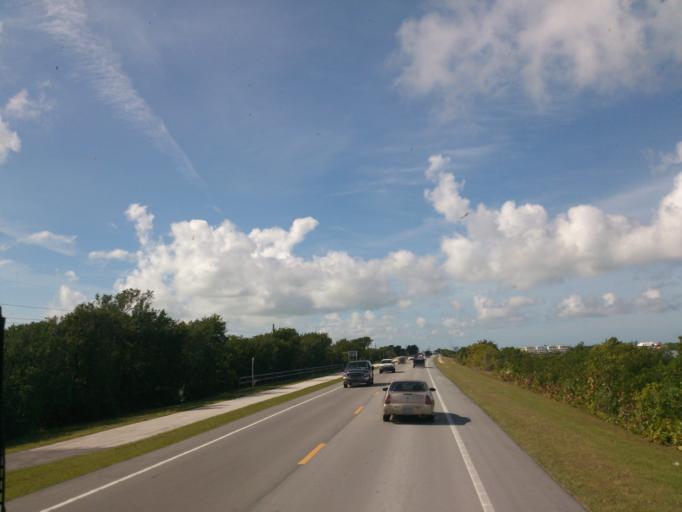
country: US
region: Florida
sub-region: Monroe County
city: Big Pine Key
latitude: 24.6683
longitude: -81.3781
